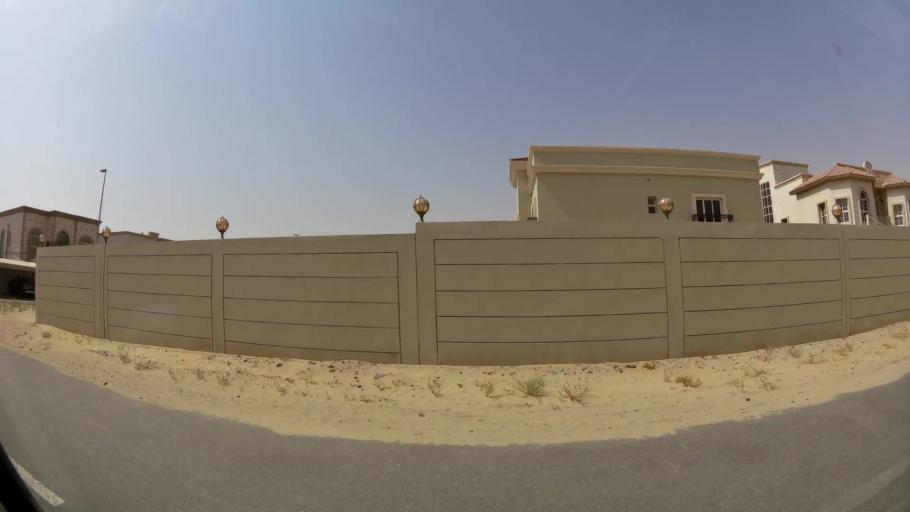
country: AE
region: Ash Shariqah
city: Sharjah
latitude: 25.2434
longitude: 55.4881
